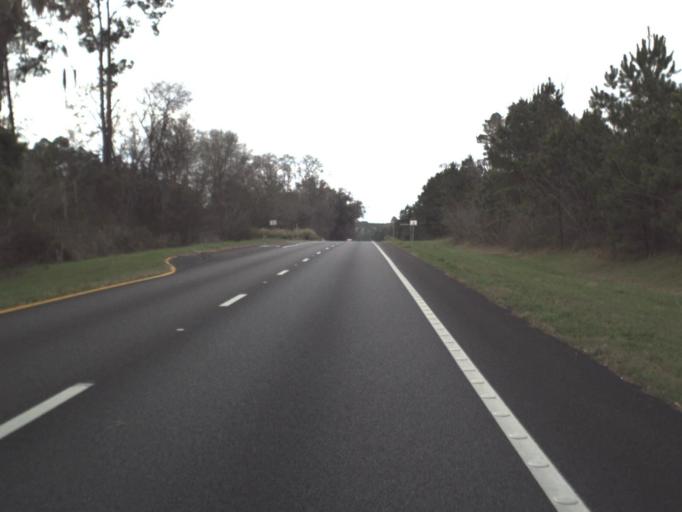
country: US
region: Florida
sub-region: Leon County
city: Tallahassee
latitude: 30.6326
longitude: -84.1689
